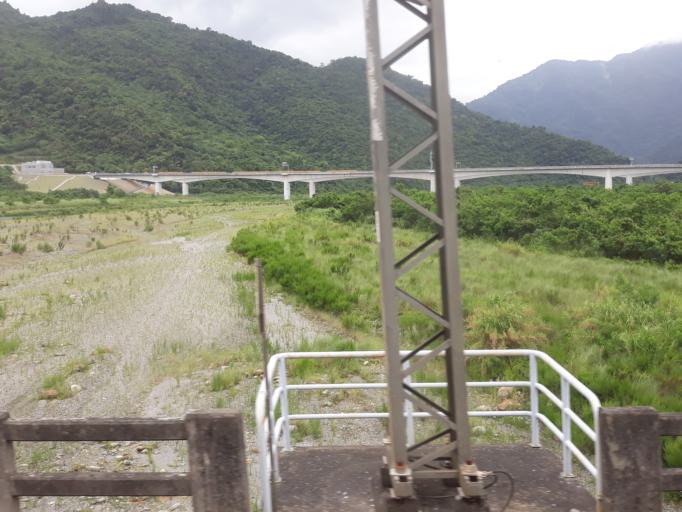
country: TW
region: Taiwan
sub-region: Yilan
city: Yilan
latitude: 24.4419
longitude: 121.7795
